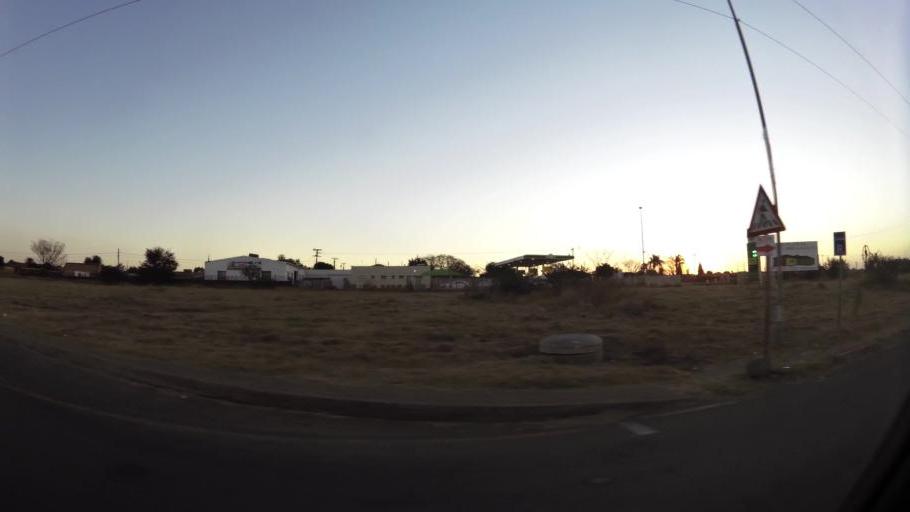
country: ZA
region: North-West
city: Ga-Rankuwa
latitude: -25.6086
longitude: 28.0049
